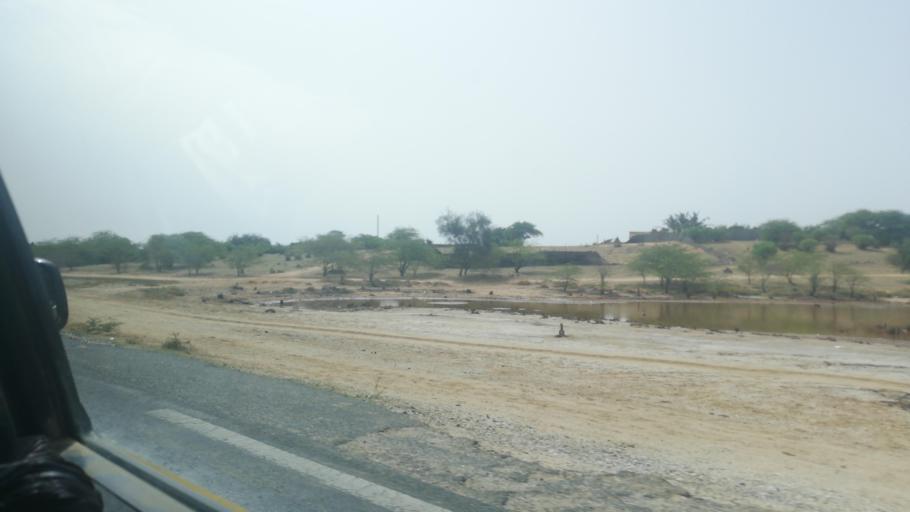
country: SN
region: Saint-Louis
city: Saint-Louis
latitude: 16.0734
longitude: -16.3866
